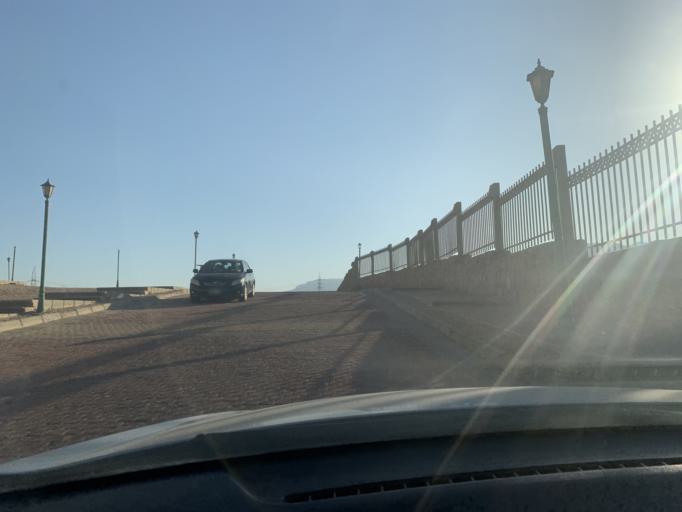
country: EG
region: As Suways
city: Ain Sukhna
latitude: 29.3745
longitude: 32.5696
